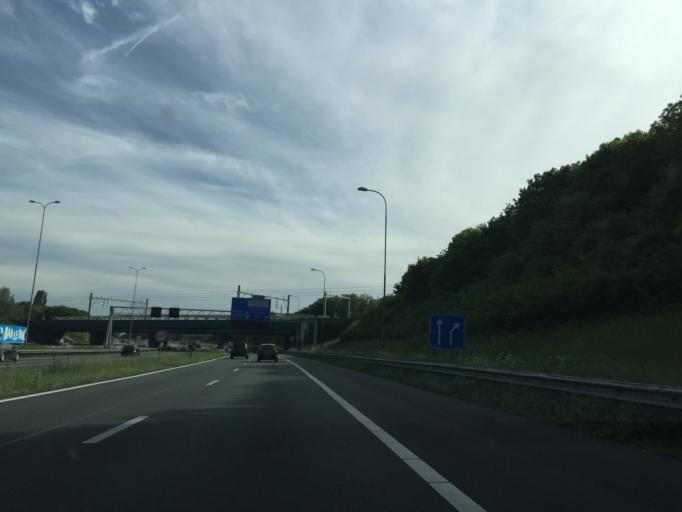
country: NL
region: Utrecht
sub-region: Gemeente Utrecht
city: Lunetten
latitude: 52.0657
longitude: 5.1459
